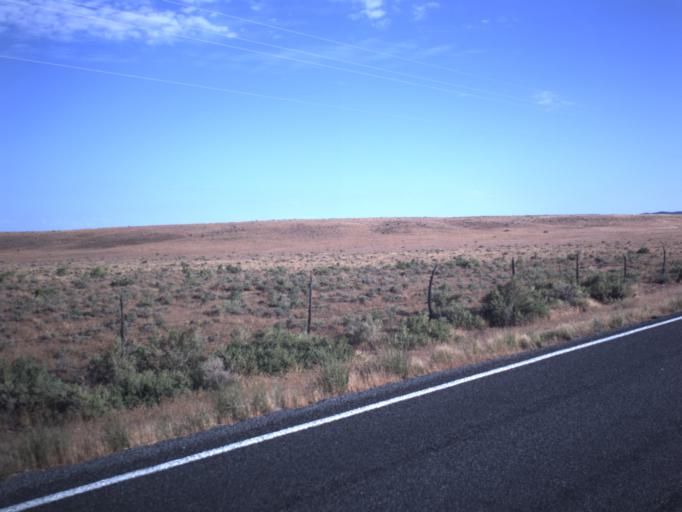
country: US
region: Utah
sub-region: Iron County
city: Enoch
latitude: 37.8832
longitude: -113.0316
